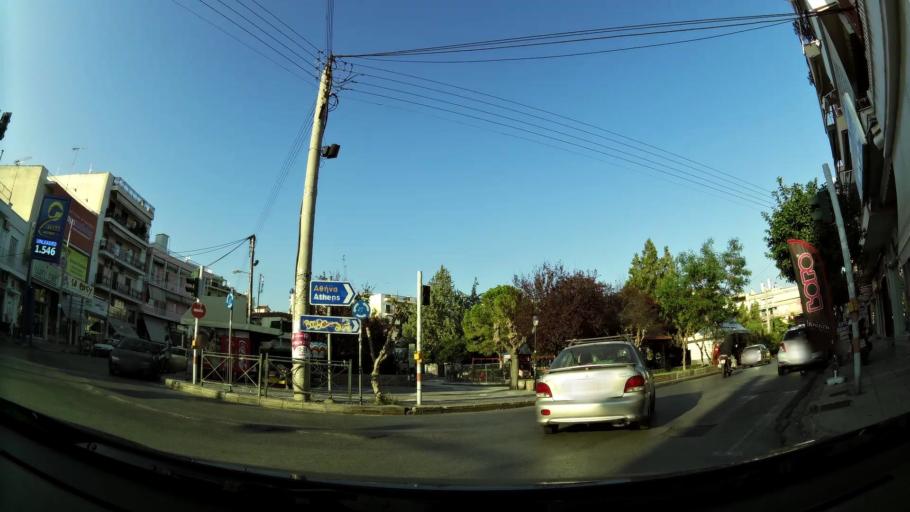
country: GR
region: Attica
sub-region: Nomos Piraios
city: Korydallos
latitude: 37.9753
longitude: 23.6409
